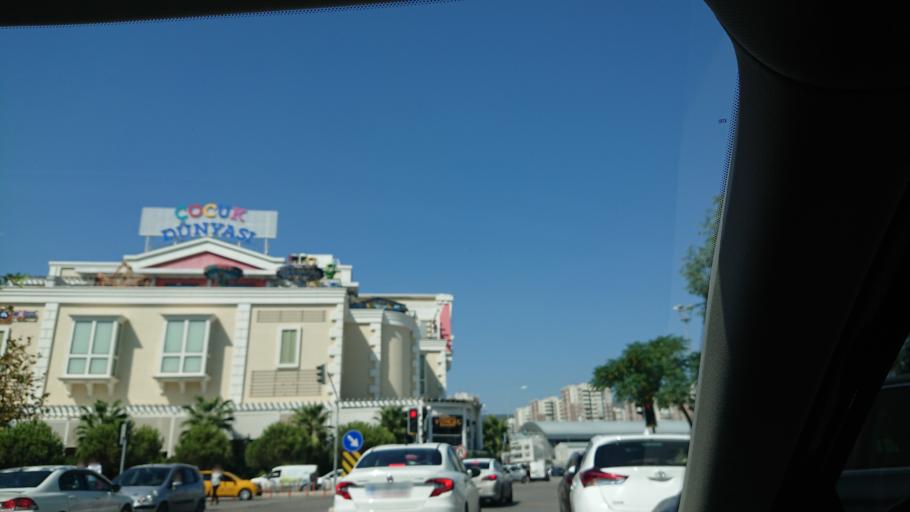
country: TR
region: Izmir
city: Karsiyaka
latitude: 38.4720
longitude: 27.0755
